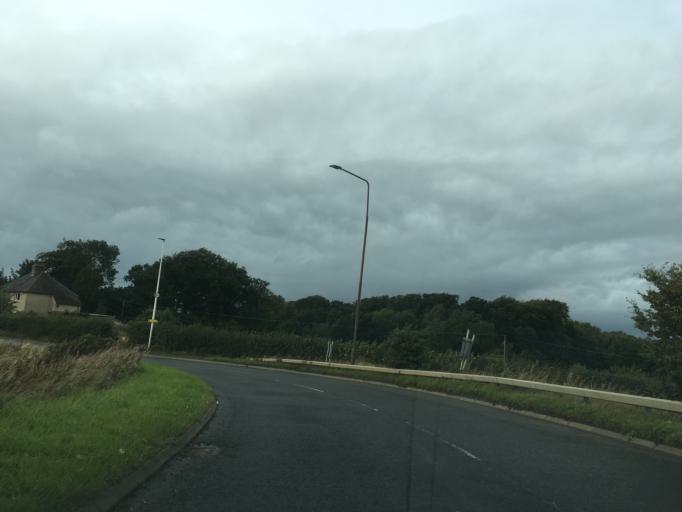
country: GB
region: Scotland
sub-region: West Lothian
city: Kirknewton
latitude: 55.9007
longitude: -3.4190
